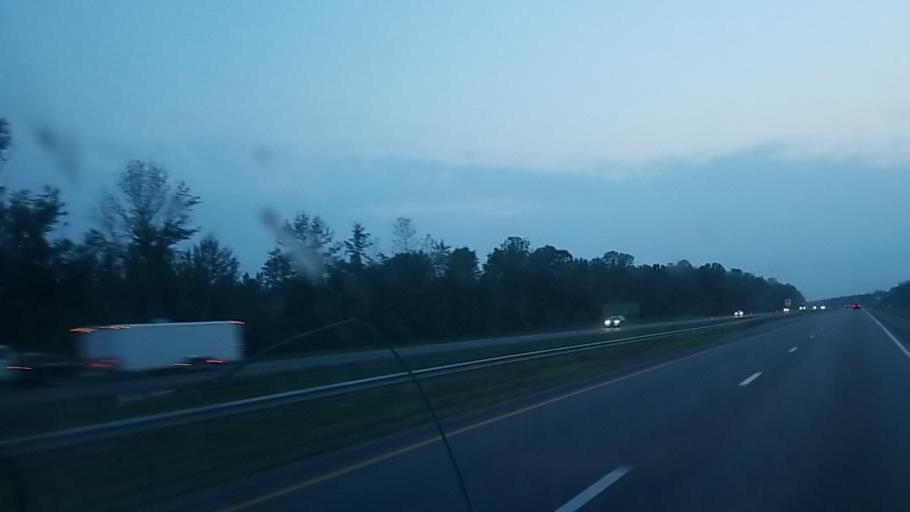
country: US
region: New York
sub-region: Madison County
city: Canastota
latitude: 43.0930
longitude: -75.7911
